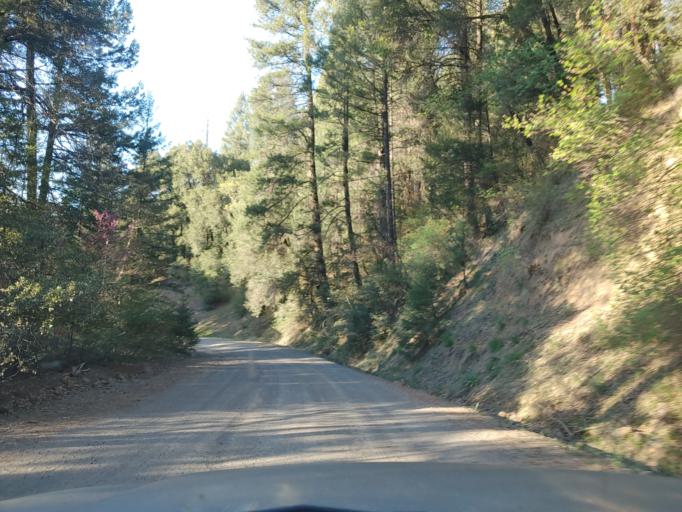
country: US
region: California
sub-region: Shasta County
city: Bella Vista
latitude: 40.8140
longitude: -122.0060
